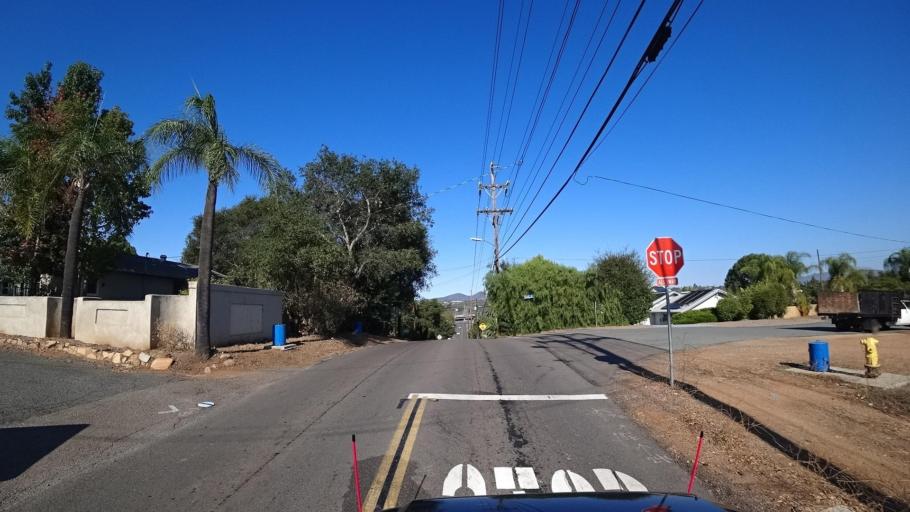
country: US
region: California
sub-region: San Diego County
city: Escondido
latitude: 33.0912
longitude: -117.0755
